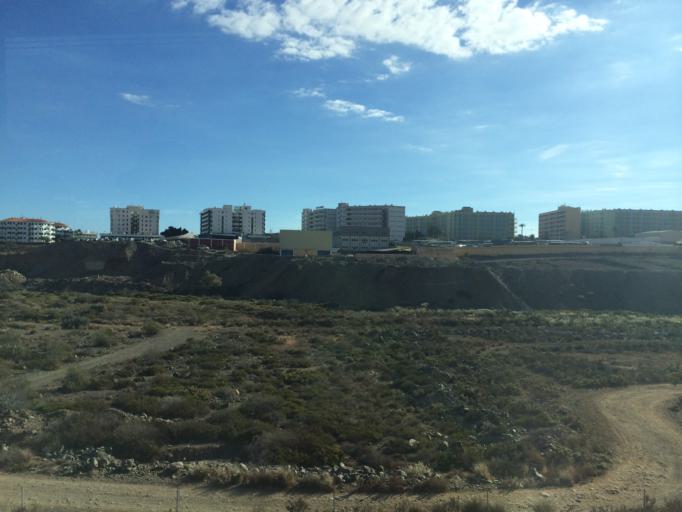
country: ES
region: Canary Islands
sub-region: Provincia de Las Palmas
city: Playa del Ingles
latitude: 27.7678
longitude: -15.5661
